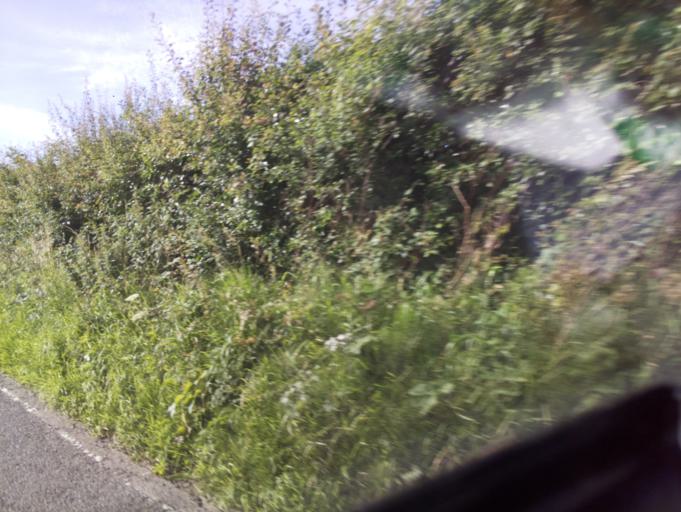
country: GB
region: England
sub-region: South Gloucestershire
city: Cold Ashton
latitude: 51.4358
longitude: -2.4078
